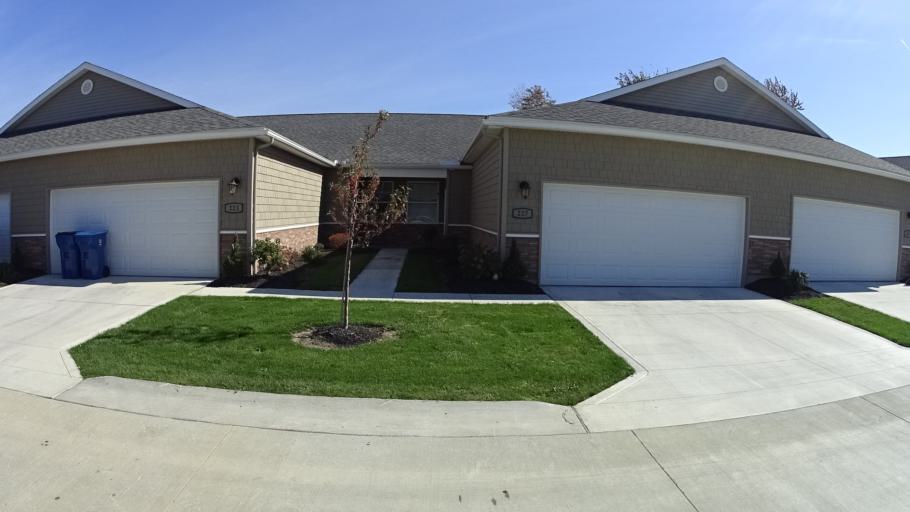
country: US
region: Ohio
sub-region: Lorain County
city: Vermilion-on-the-Lake
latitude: 41.4260
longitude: -82.3030
